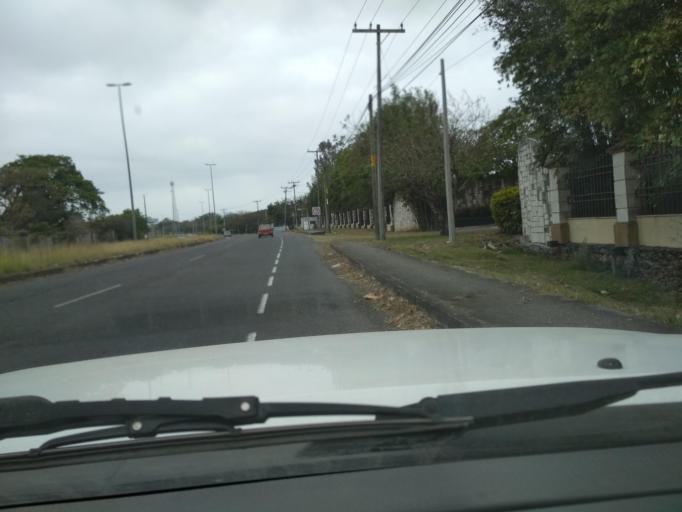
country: MX
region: Veracruz
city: Boca del Rio
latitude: 19.0903
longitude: -96.1158
